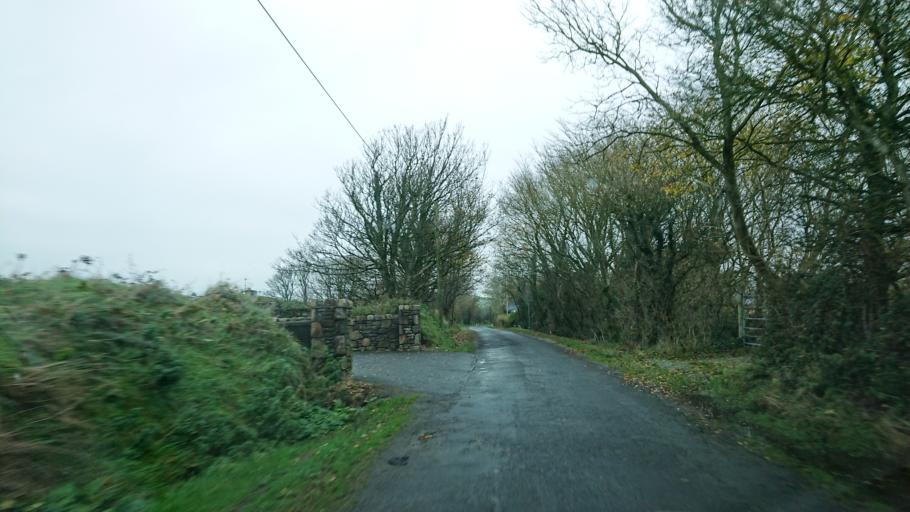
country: IE
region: Munster
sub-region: Waterford
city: Dunmore East
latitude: 52.1728
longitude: -7.0176
